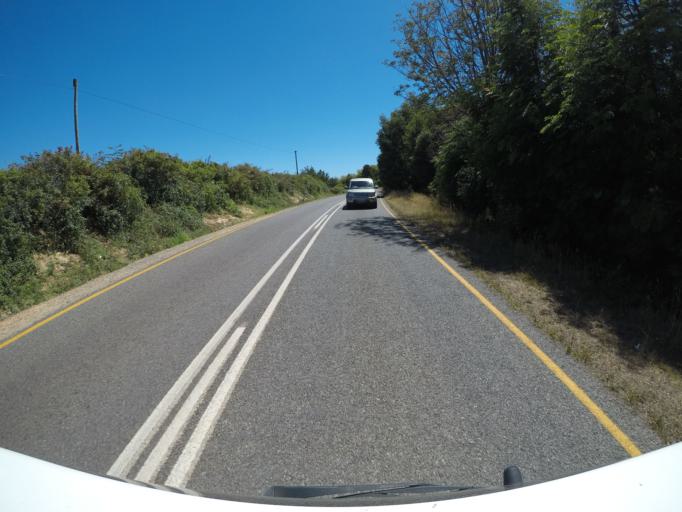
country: ZA
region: Western Cape
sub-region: Overberg District Municipality
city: Grabouw
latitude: -34.2126
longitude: 19.0519
